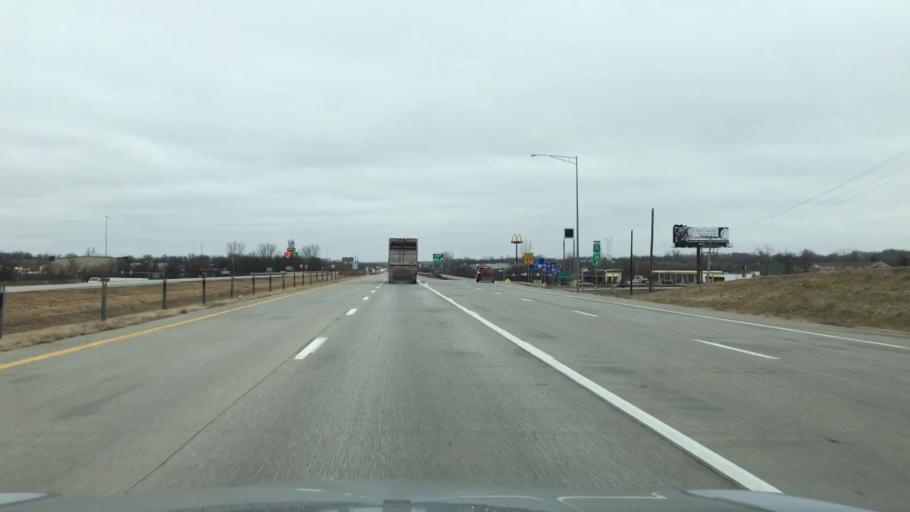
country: US
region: Missouri
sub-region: Clay County
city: Kearney
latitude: 39.3654
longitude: -94.3724
